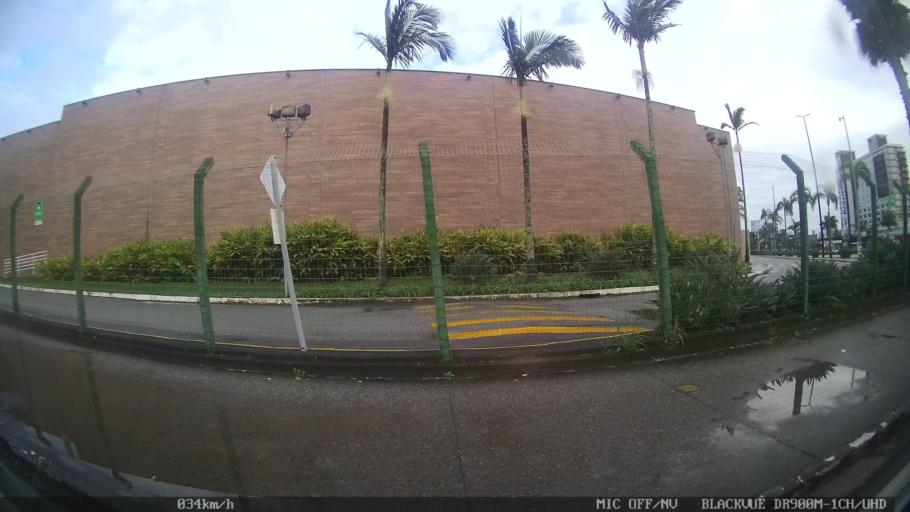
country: BR
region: Santa Catarina
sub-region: Sao Jose
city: Campinas
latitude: -27.5852
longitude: -48.6133
